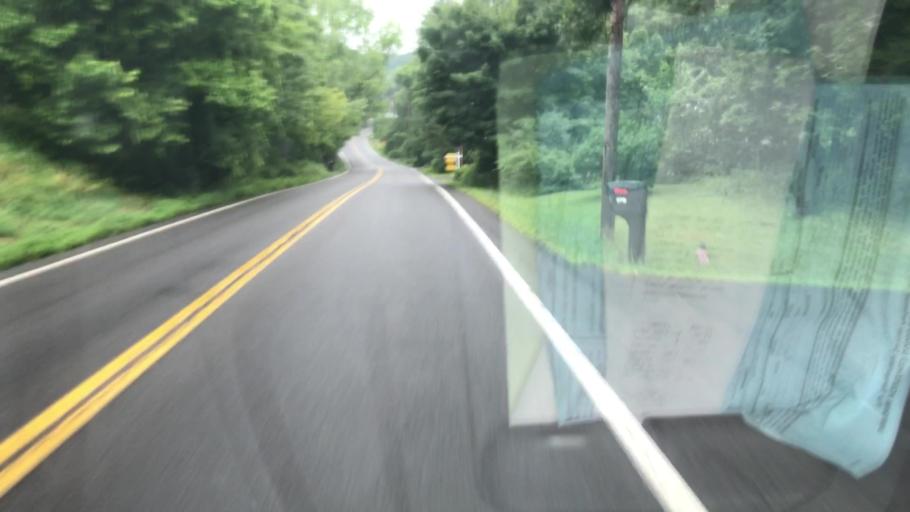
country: US
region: New York
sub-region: Onondaga County
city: Manlius
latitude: 42.9994
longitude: -75.9931
